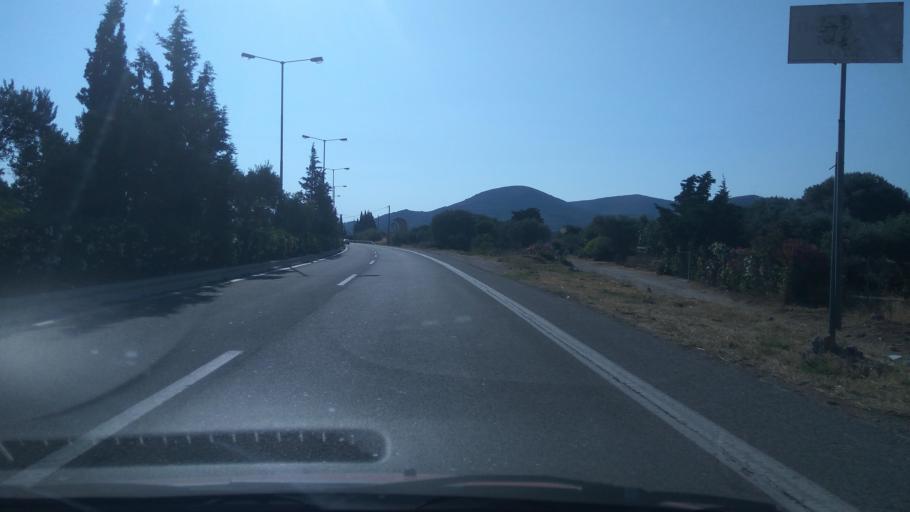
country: GR
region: Attica
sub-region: Nomarchia Anatolikis Attikis
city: Keratea
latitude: 37.7998
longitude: 24.0017
